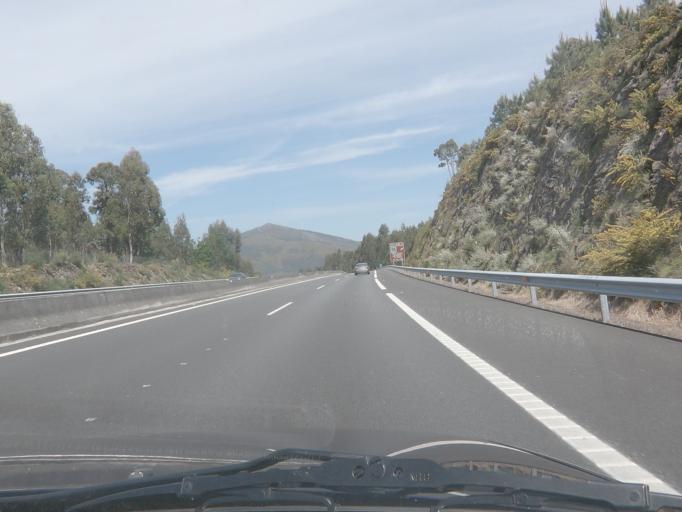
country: ES
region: Galicia
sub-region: Provincia de Pontevedra
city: Valga
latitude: 42.7176
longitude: -8.6428
